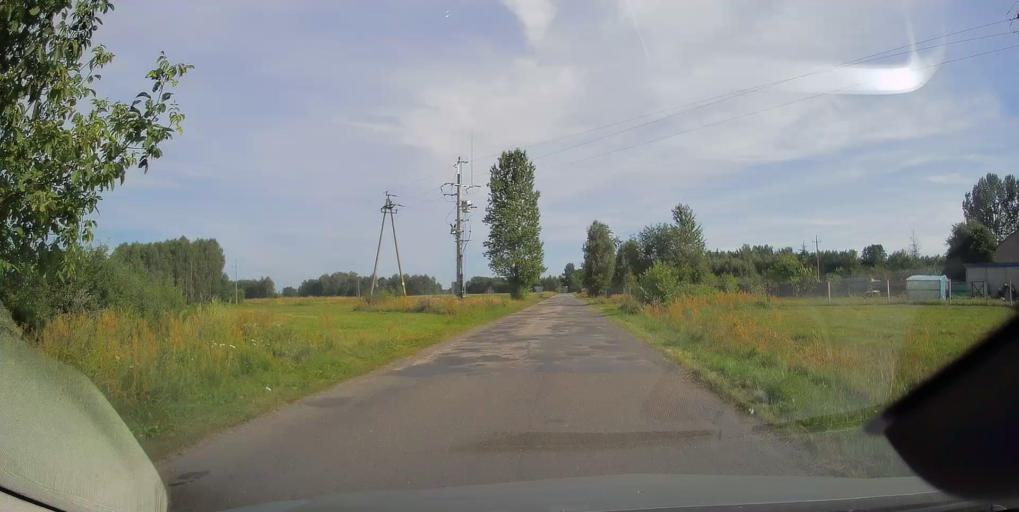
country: PL
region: Lodz Voivodeship
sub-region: Powiat opoczynski
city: Mniszkow
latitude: 51.4224
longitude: 20.0251
